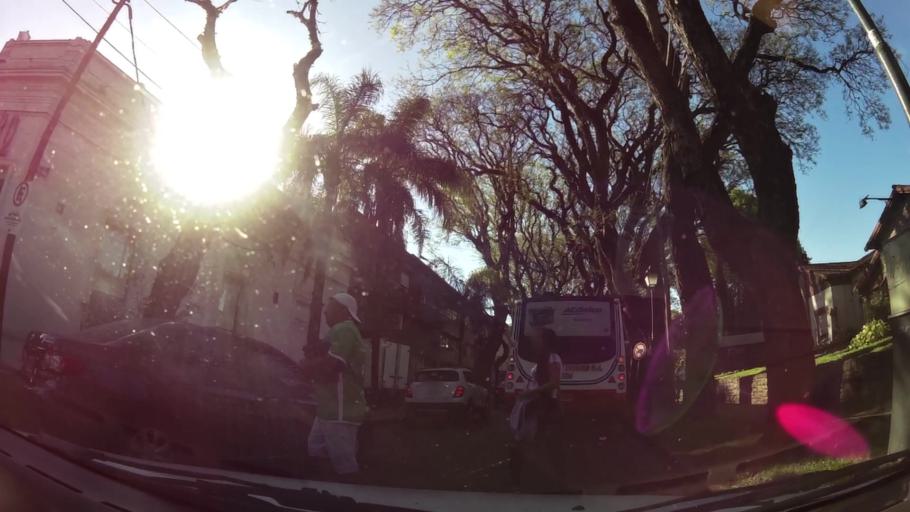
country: AR
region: Buenos Aires
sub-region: Partido de San Isidro
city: San Isidro
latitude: -34.4712
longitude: -58.5067
